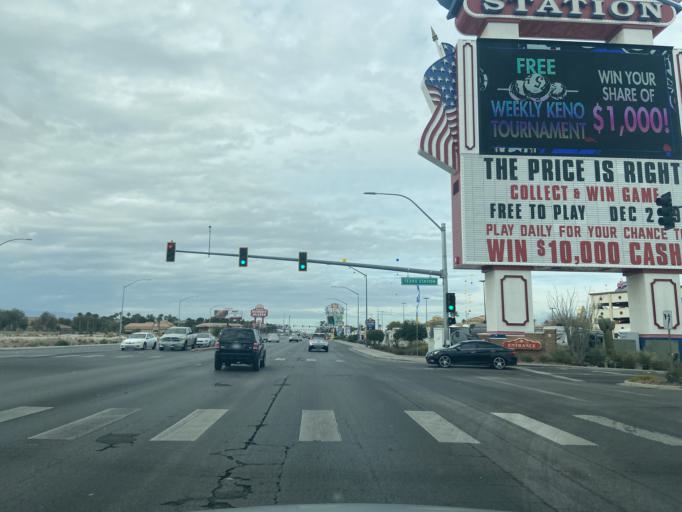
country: US
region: Nevada
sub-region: Clark County
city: Las Vegas
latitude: 36.1979
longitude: -115.1944
